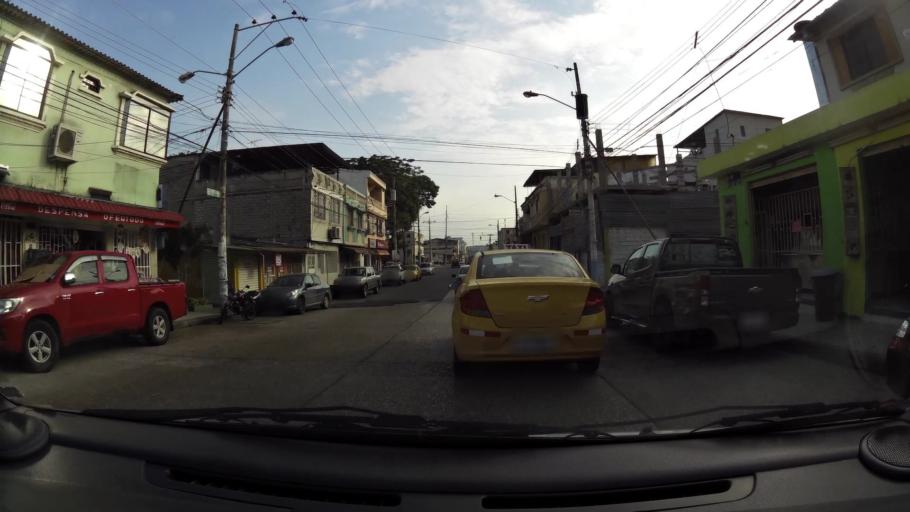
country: EC
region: Guayas
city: Eloy Alfaro
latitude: -2.1352
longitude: -79.8928
